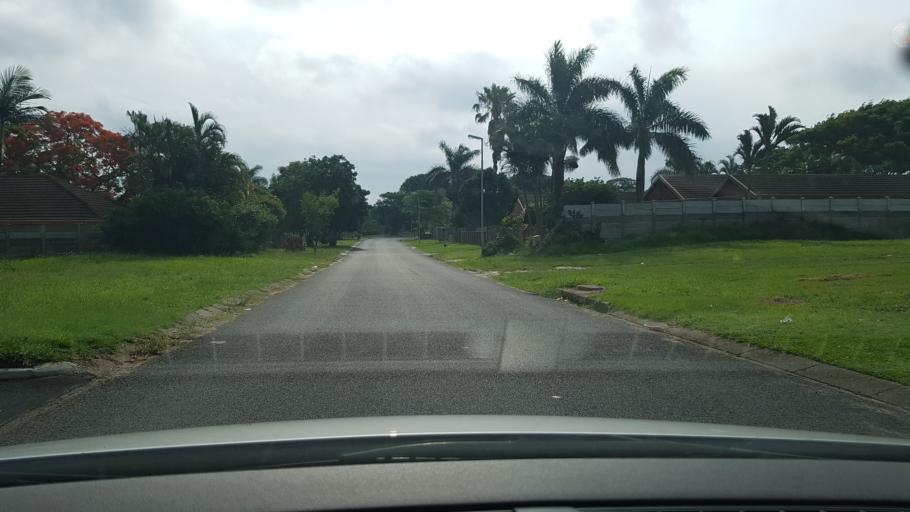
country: ZA
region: KwaZulu-Natal
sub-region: uThungulu District Municipality
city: Richards Bay
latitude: -28.7626
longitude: 32.0574
